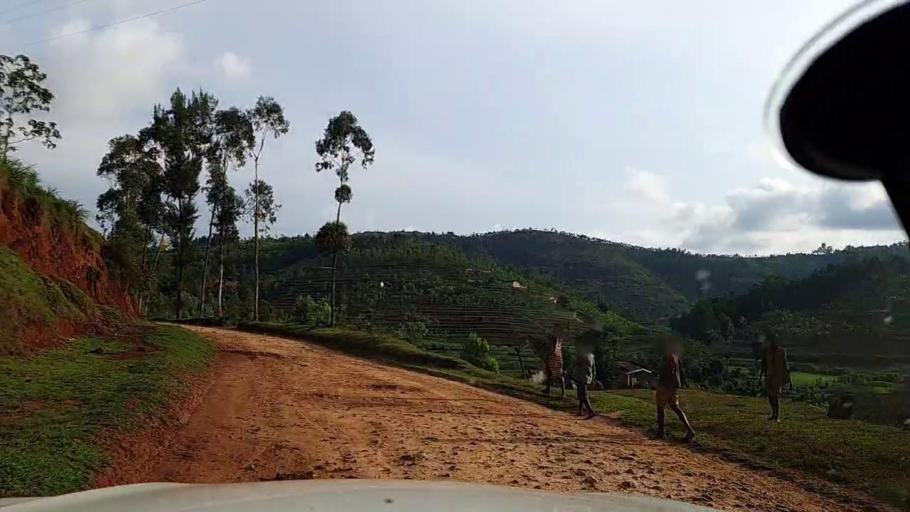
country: RW
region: Southern Province
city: Gitarama
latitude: -2.1796
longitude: 29.5585
